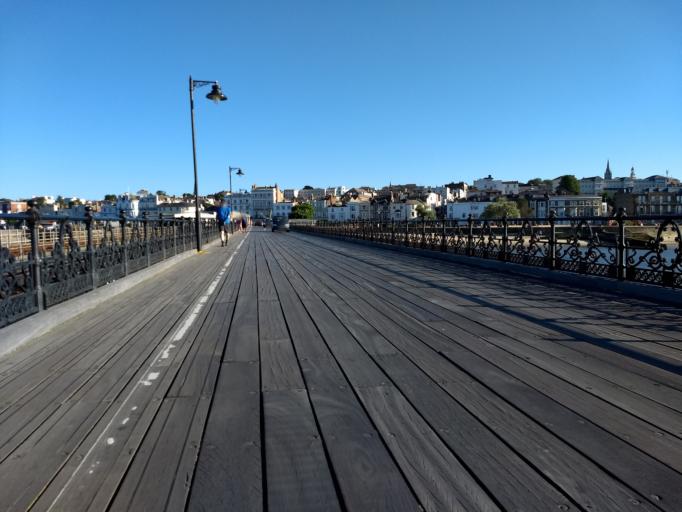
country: GB
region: England
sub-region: Isle of Wight
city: Ryde
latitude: 50.7346
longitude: -1.1604
